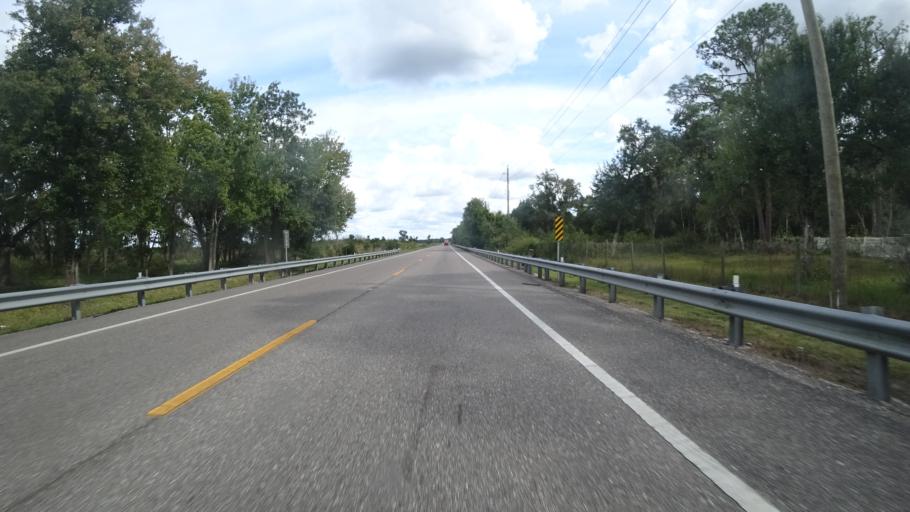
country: US
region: Florida
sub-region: Sarasota County
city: Lake Sarasota
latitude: 27.3870
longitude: -82.2626
